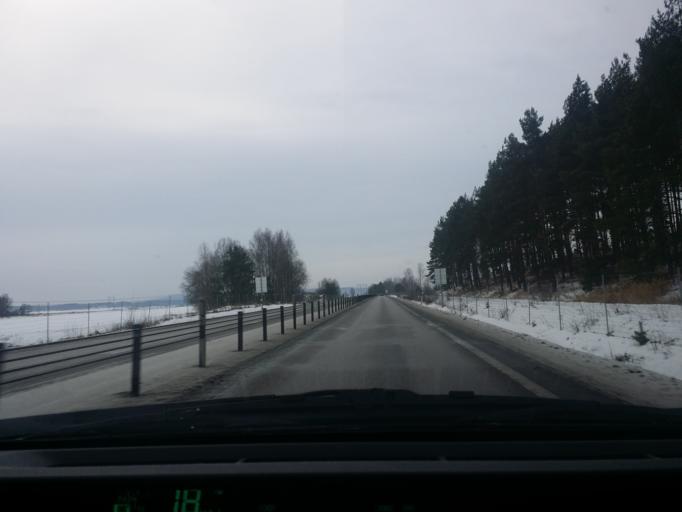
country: SE
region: Vaestra Goetaland
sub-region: Skovde Kommun
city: Stopen
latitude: 58.5757
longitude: 13.8006
